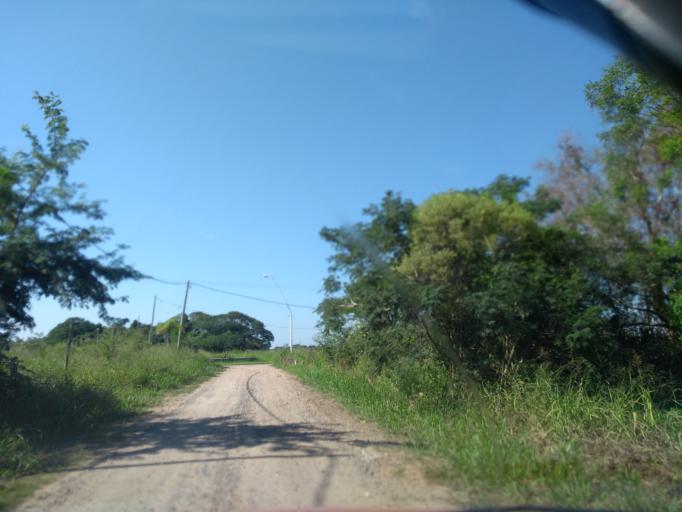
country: AR
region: Chaco
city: Barranqueras
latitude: -27.4307
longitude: -58.9352
